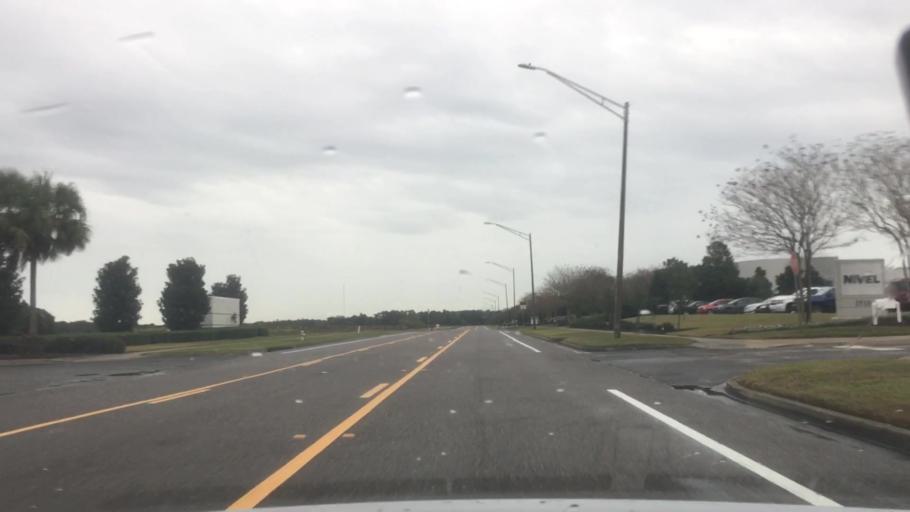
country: US
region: Florida
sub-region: Duval County
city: Jacksonville
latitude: 30.4509
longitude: -81.5696
